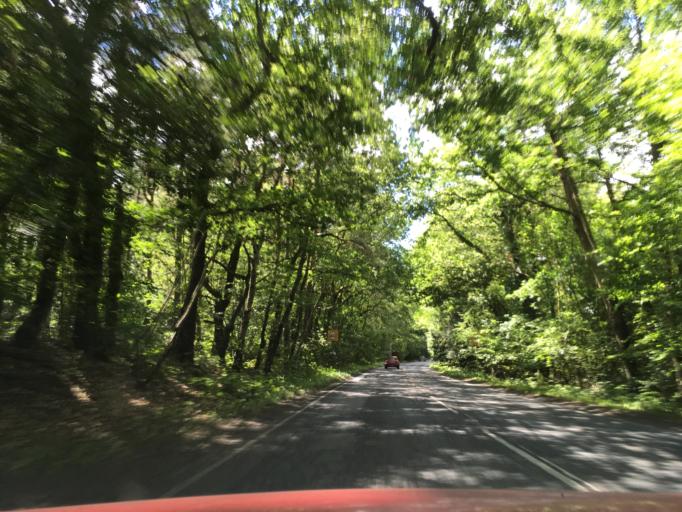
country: GB
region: England
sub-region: Hampshire
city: Highclere
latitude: 51.3572
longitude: -1.3664
